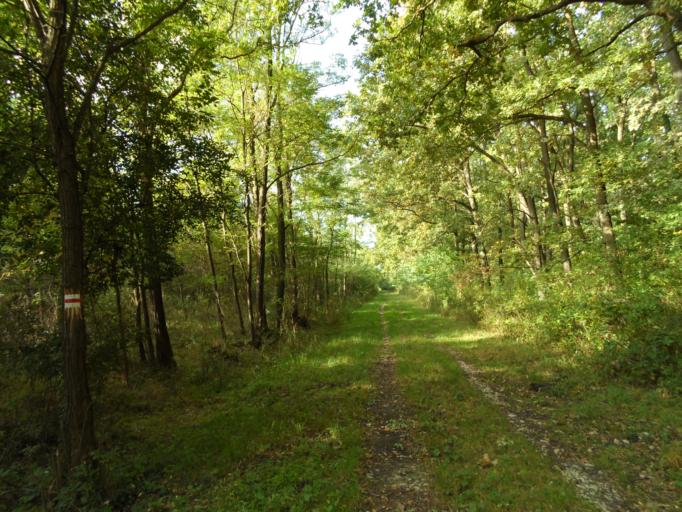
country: HU
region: Veszprem
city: Devecser
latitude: 47.1999
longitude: 17.4399
